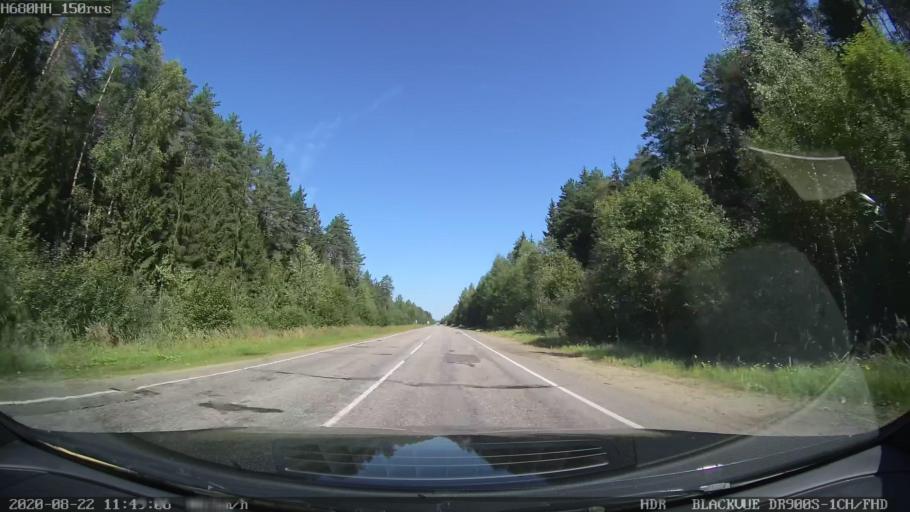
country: RU
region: Tverskaya
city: Sakharovo
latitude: 57.0713
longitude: 36.1101
